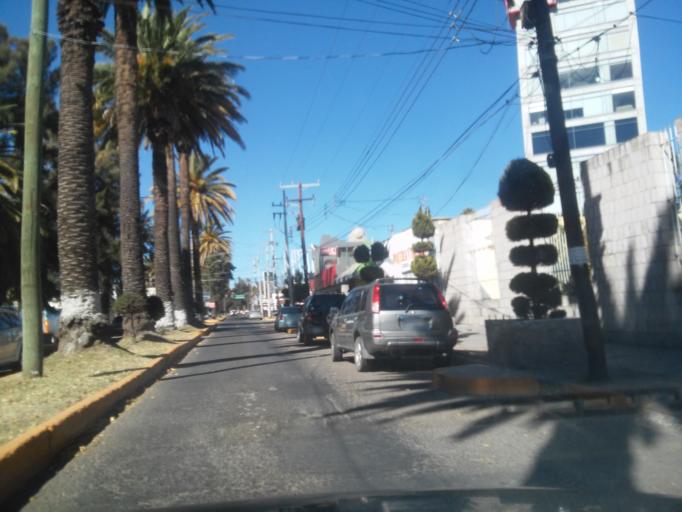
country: MX
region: Durango
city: Victoria de Durango
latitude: 24.0234
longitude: -104.6789
